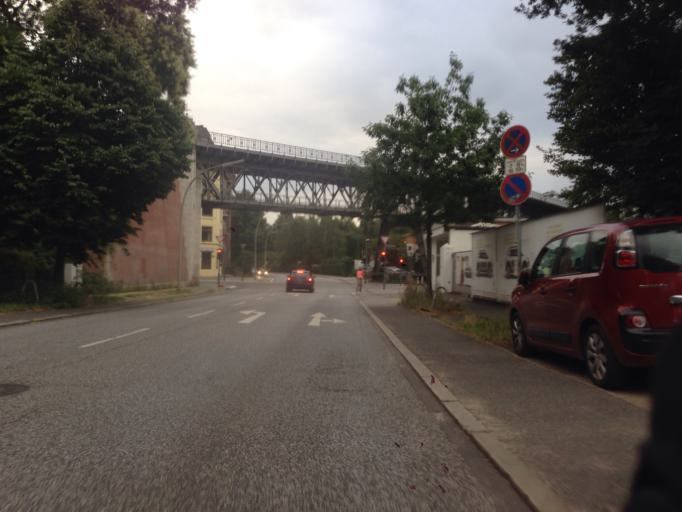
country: DE
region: Hamburg
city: Barmbek-Nord
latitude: 53.5920
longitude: 10.0385
